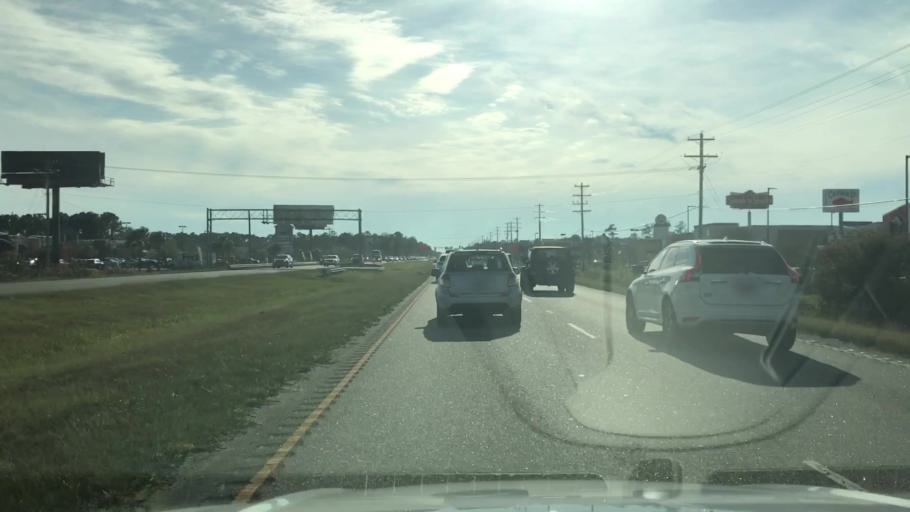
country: US
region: South Carolina
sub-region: Horry County
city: Surfside Beach
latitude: 33.6420
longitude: -78.9881
